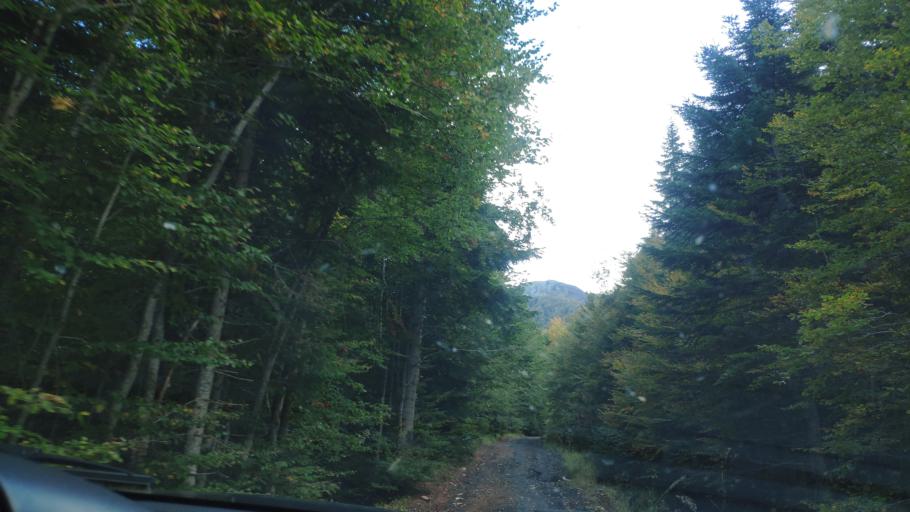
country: AL
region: Korce
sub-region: Rrethi i Devollit
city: Miras
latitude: 40.3352
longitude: 20.9004
